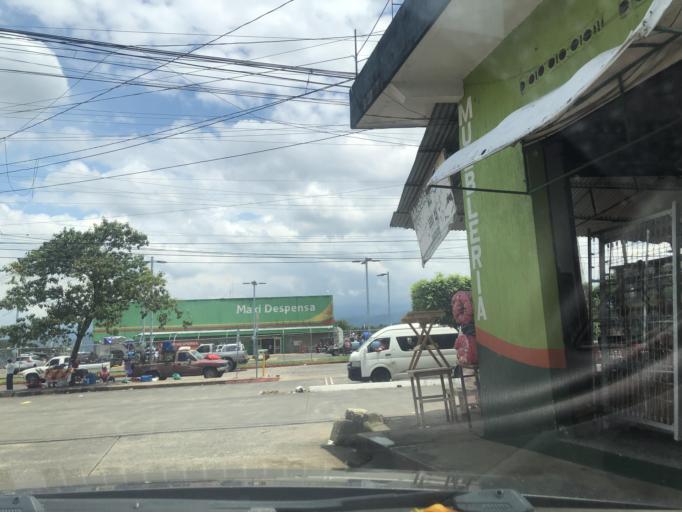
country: GT
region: Quetzaltenango
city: Coatepeque
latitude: 14.7102
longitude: -91.8679
